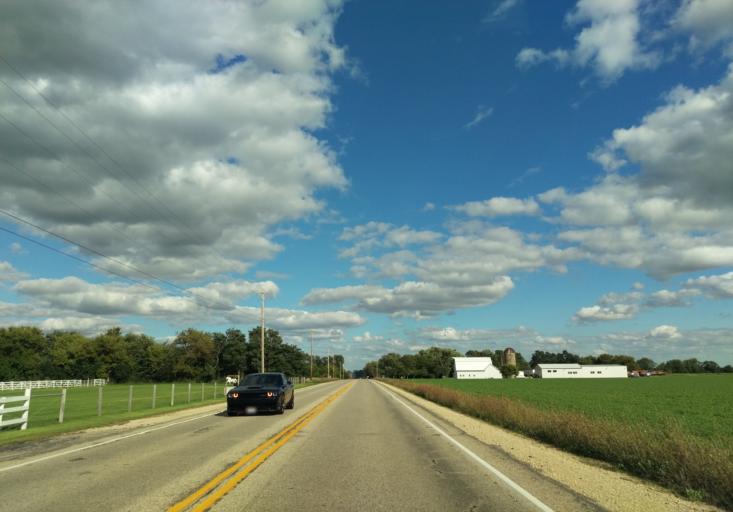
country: US
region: Wisconsin
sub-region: Rock County
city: Janesville
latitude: 42.7303
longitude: -89.0838
